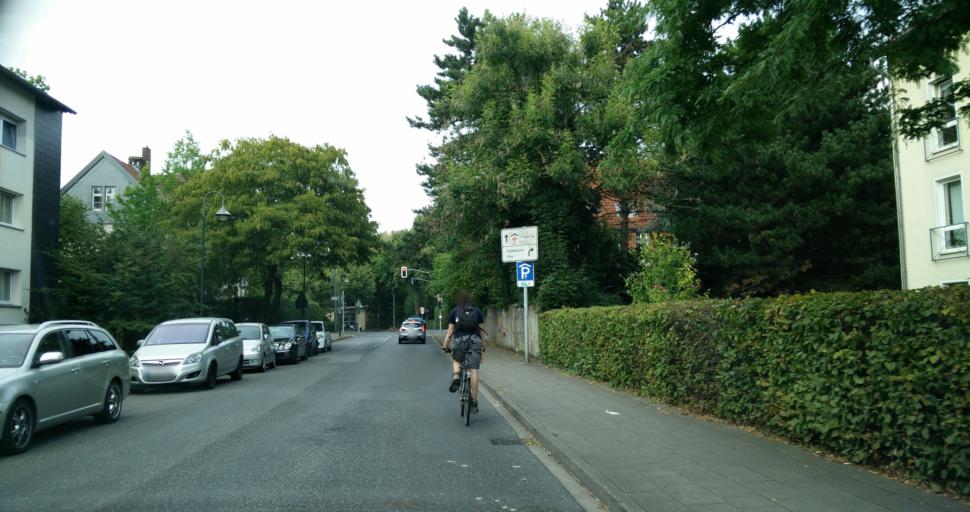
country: DE
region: North Rhine-Westphalia
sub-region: Regierungsbezirk Dusseldorf
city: Meerbusch
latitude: 51.2982
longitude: 6.7424
